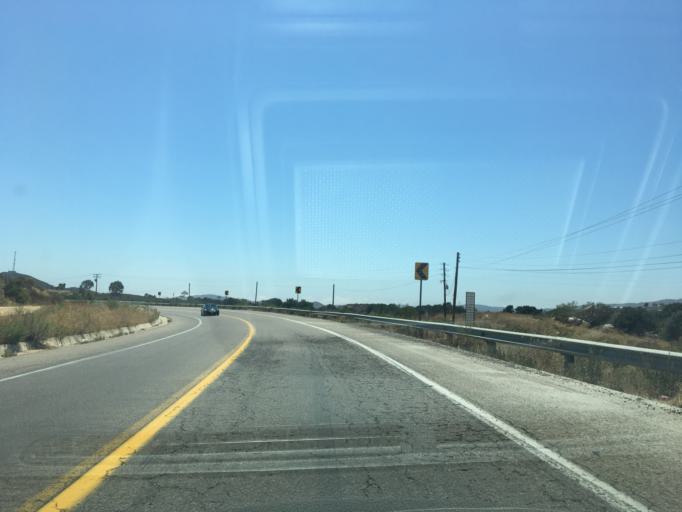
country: MX
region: Baja California
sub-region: Ensenada
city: Rancho Verde
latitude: 32.0251
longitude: -116.6254
